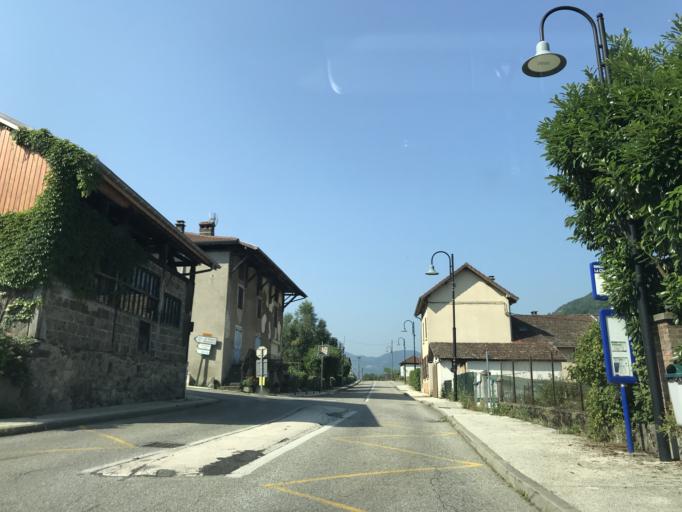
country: FR
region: Rhone-Alpes
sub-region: Departement de l'Isere
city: Allevard
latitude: 45.4224
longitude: 6.0951
